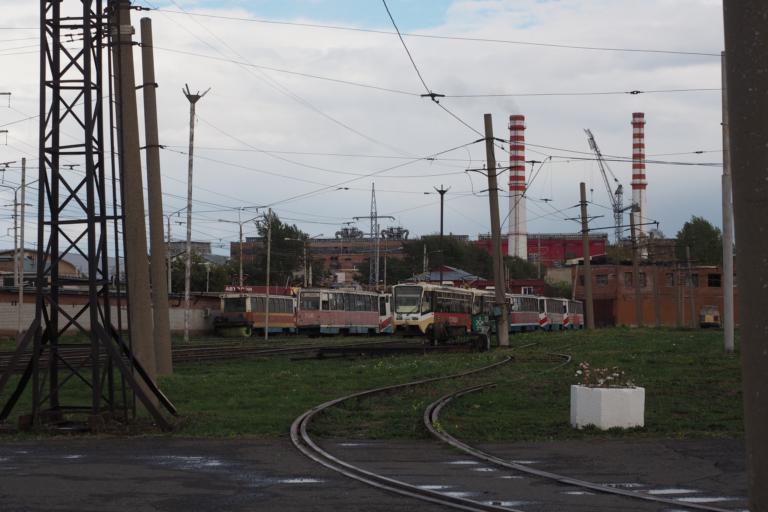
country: RU
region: Tomsk
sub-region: Tomskiy Rayon
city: Tomsk
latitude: 56.4705
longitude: 84.9820
